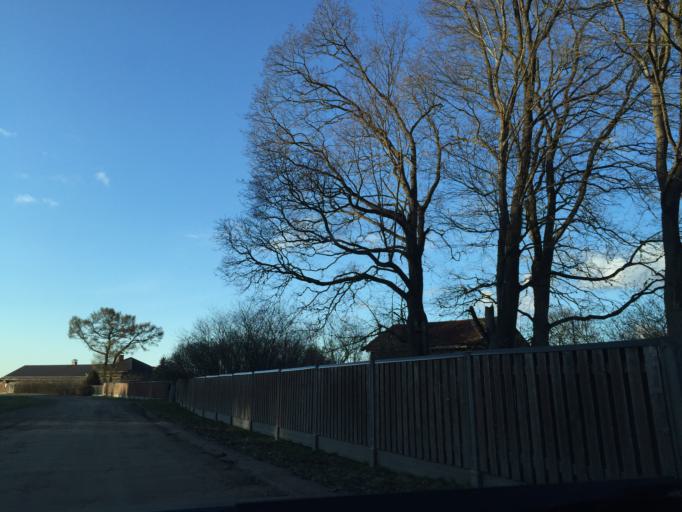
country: LV
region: Kekava
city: Kekava
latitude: 56.8717
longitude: 24.2205
